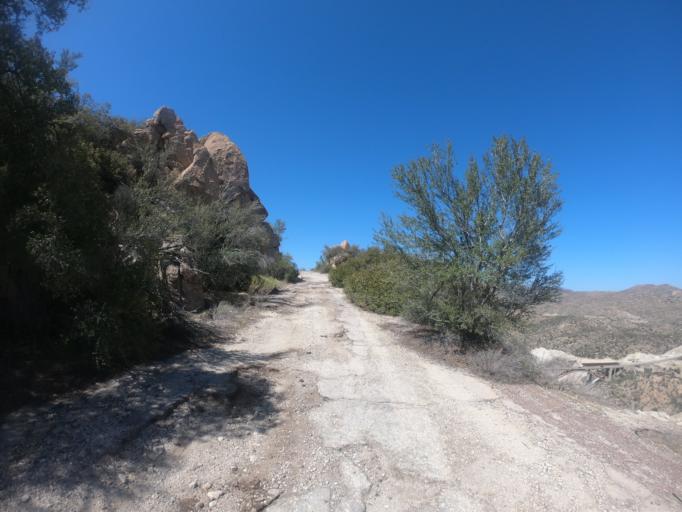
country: US
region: Arizona
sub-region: Gila County
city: Miami
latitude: 33.3579
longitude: -110.9578
